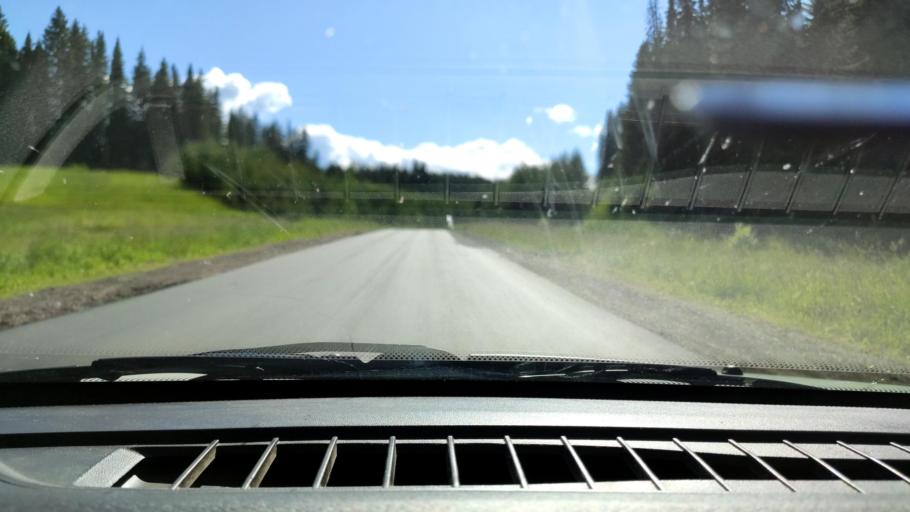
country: RU
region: Perm
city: Uinskoye
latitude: 57.1152
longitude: 56.5455
